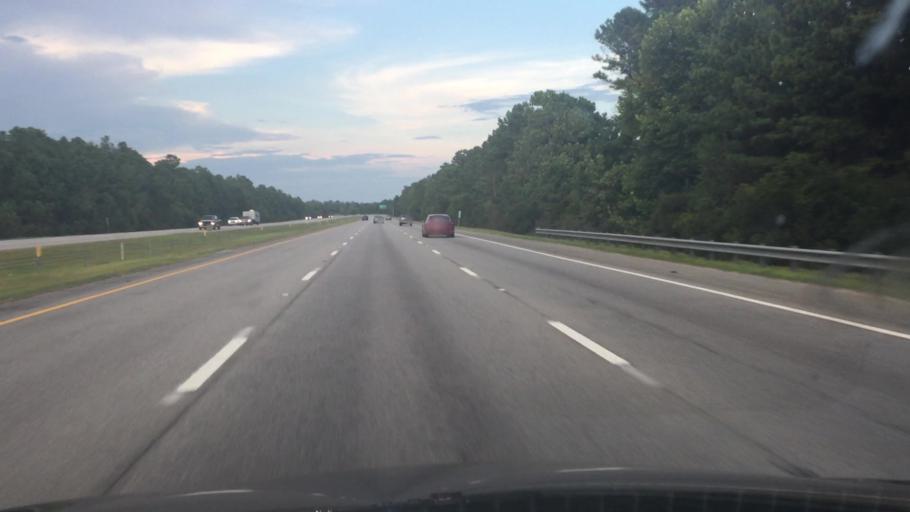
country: US
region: South Carolina
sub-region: Horry County
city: Myrtle Beach
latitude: 33.7769
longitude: -78.8135
